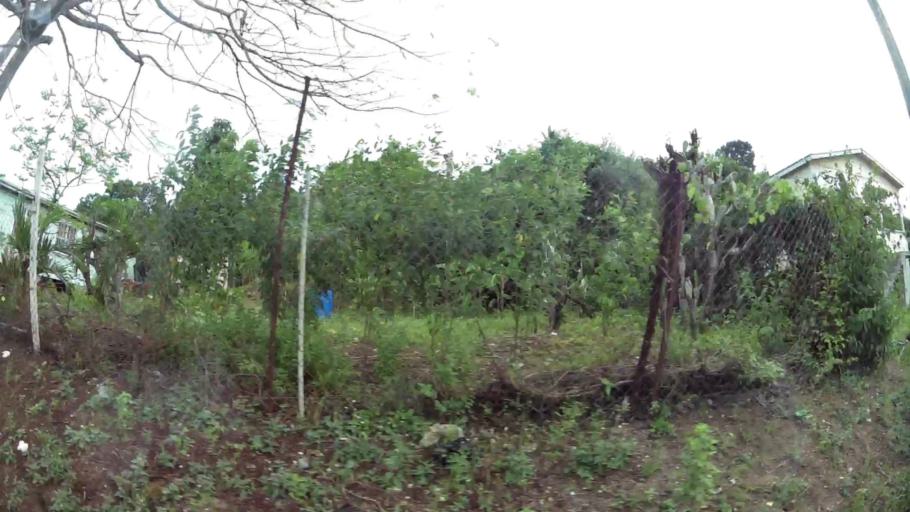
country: AG
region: Saint John
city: Saint John's
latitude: 17.1105
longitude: -61.8529
